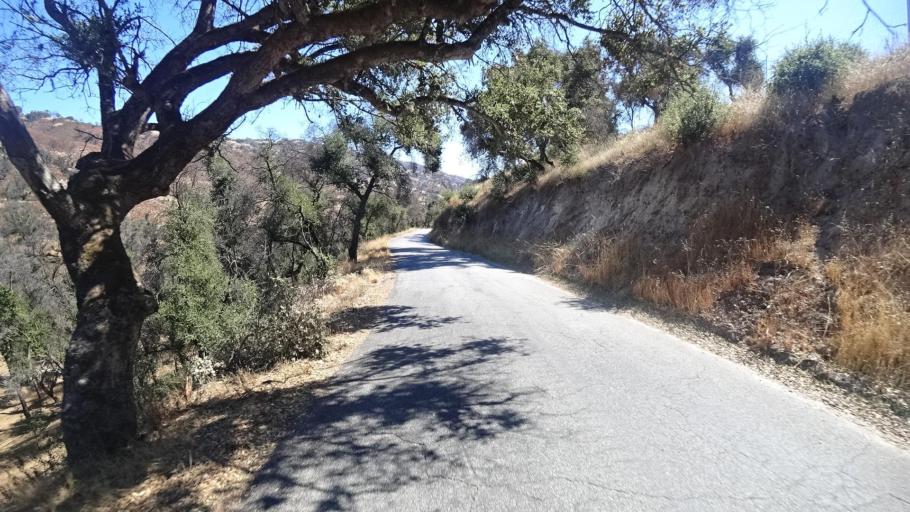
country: US
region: California
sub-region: Monterey County
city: Carmel Valley Village
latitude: 36.4231
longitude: -121.6803
